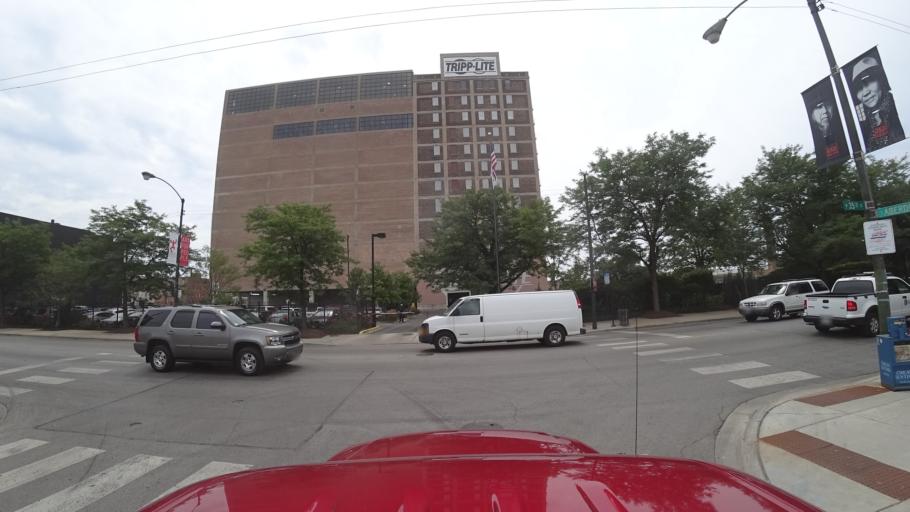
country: US
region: Illinois
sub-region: Cook County
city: Chicago
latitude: 41.8308
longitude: -87.6534
